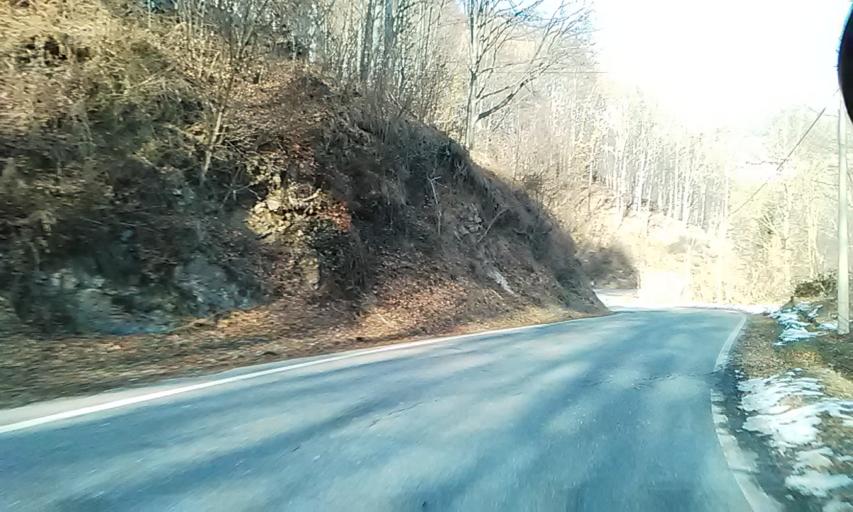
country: IT
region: Piedmont
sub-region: Provincia di Vercelli
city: Cellio
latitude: 45.7619
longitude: 8.3179
